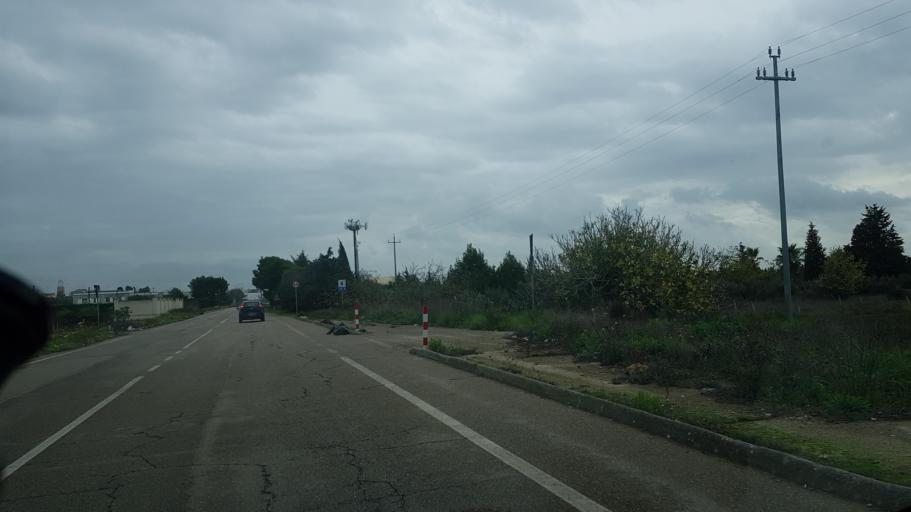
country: IT
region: Apulia
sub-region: Provincia di Lecce
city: Novoli
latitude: 40.3794
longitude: 18.0378
